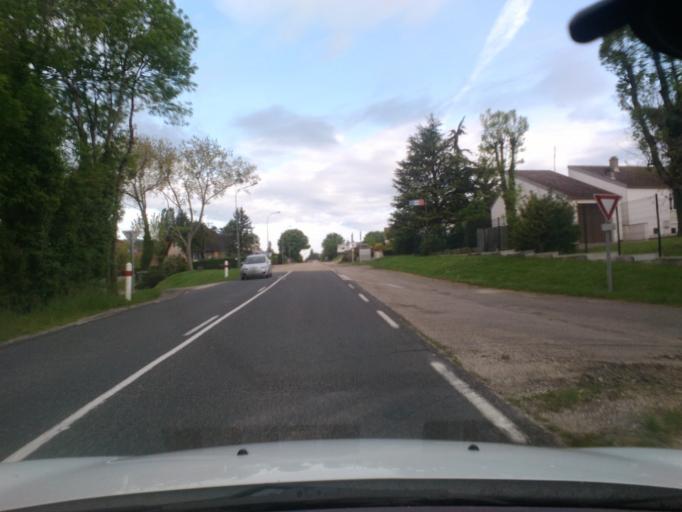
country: FR
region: Champagne-Ardenne
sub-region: Departement de la Haute-Marne
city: Lavilleneuve-au-Roi
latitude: 48.2224
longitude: 4.8947
